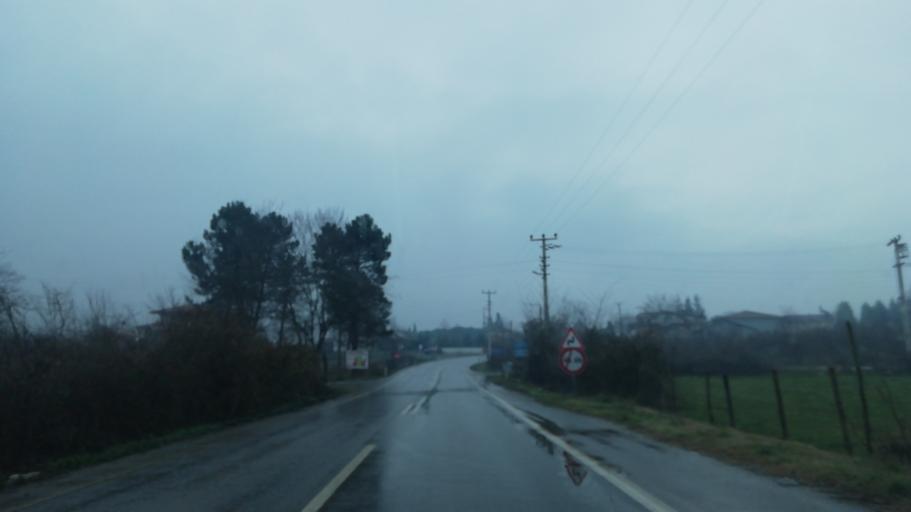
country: TR
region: Sakarya
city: Karapurcek
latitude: 40.6794
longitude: 30.5487
